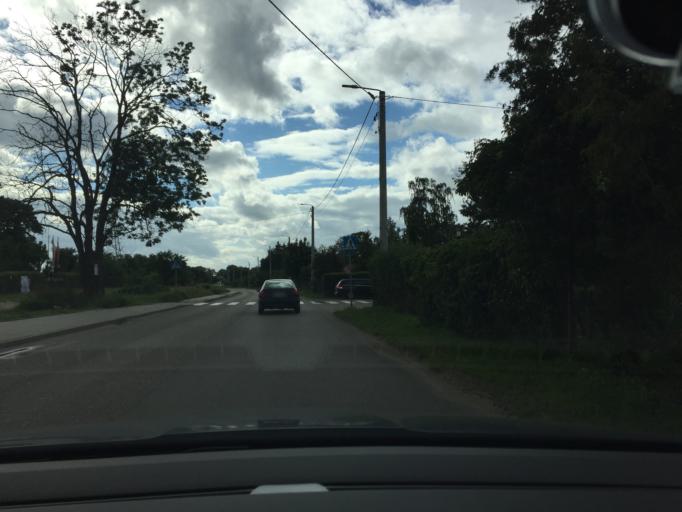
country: PL
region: Pomeranian Voivodeship
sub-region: Gdansk
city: Gdansk
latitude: 54.3592
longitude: 18.7462
